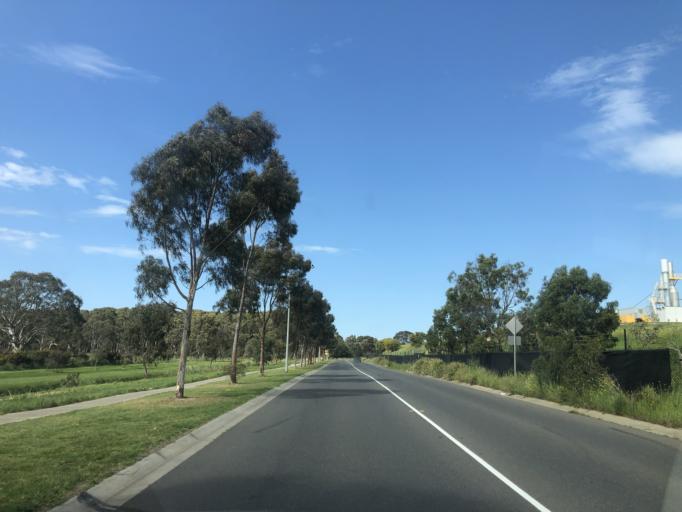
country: AU
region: Victoria
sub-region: Casey
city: Hampton Park
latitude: -38.0408
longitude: 145.2341
